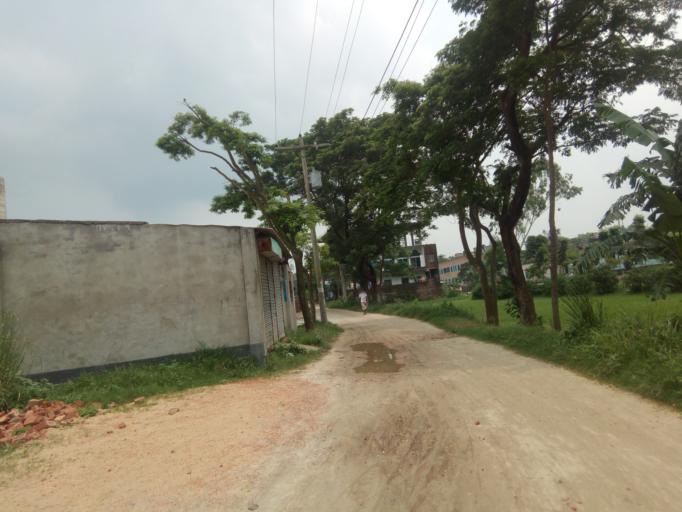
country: BD
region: Dhaka
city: Azimpur
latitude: 23.7382
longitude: 90.3380
